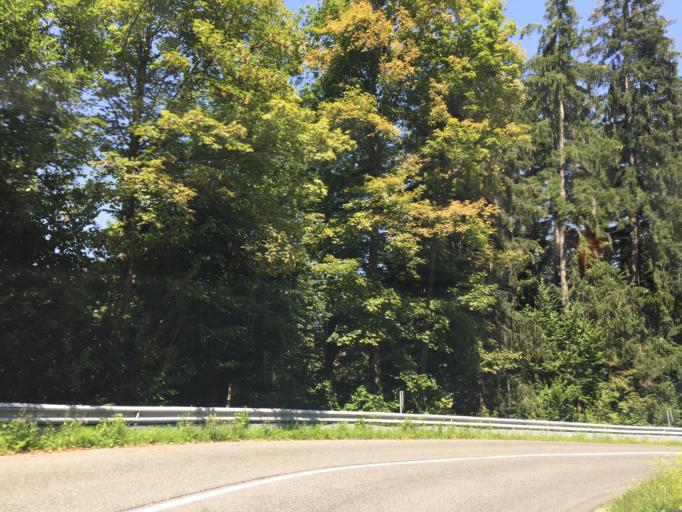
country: SI
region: Trbovlje
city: Trbovlje
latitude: 46.1900
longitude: 15.0602
